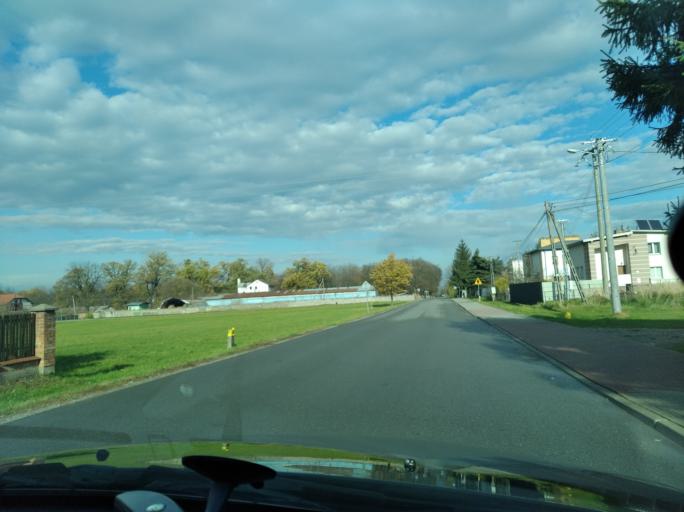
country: PL
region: Subcarpathian Voivodeship
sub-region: Powiat debicki
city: Brzeznica
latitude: 50.0539
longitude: 21.4842
